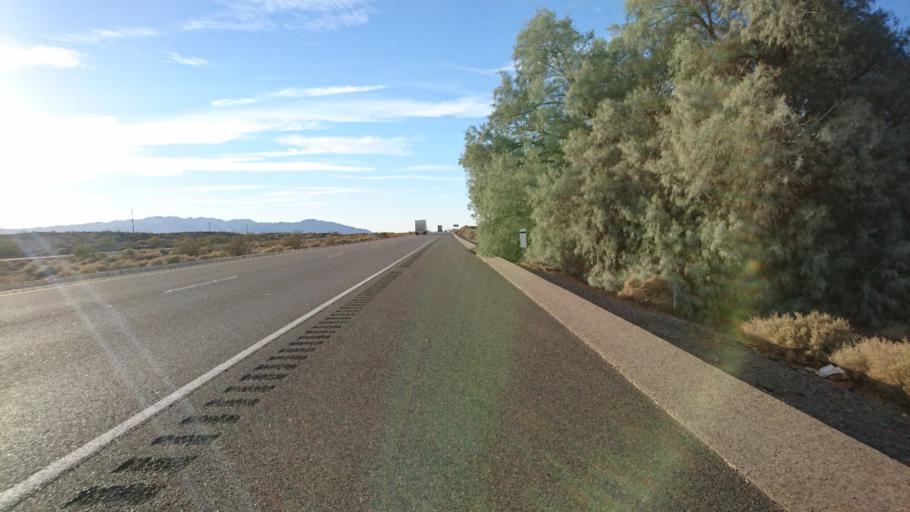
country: US
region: California
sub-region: San Bernardino County
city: Fort Irwin
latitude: 34.7950
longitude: -116.4967
